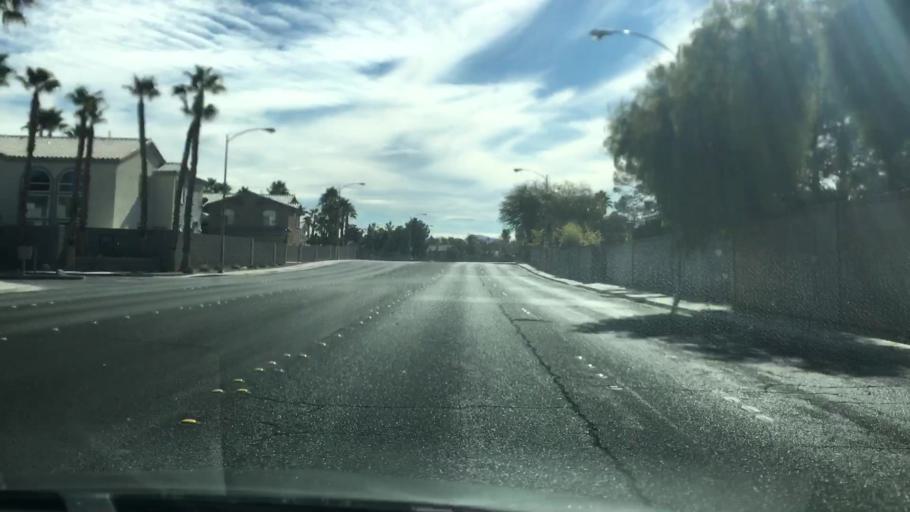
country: US
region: Nevada
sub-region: Clark County
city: Paradise
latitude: 36.0490
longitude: -115.1408
